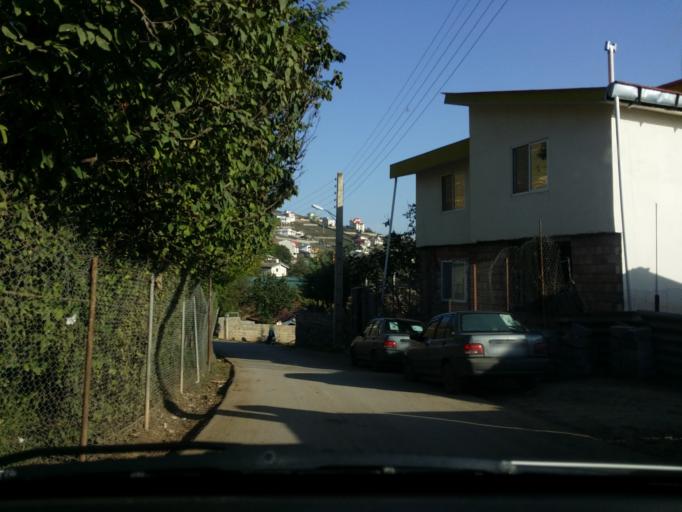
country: IR
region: Mazandaran
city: Chalus
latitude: 36.5413
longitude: 51.2351
